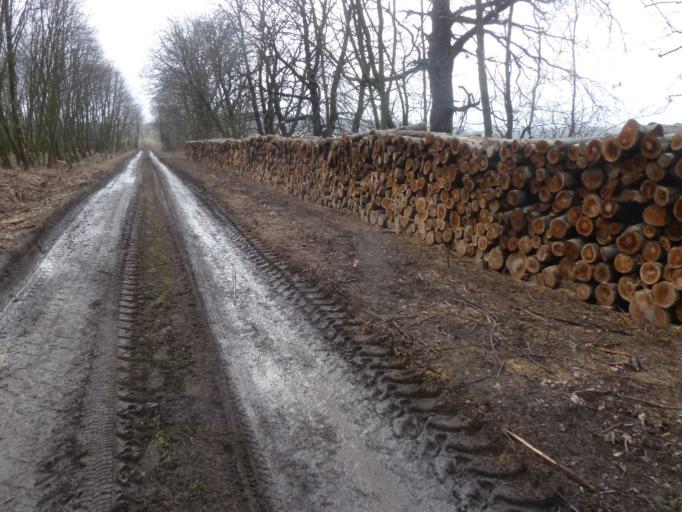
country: HU
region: Nograd
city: Somoskoujfalu
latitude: 48.1457
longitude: 19.8928
